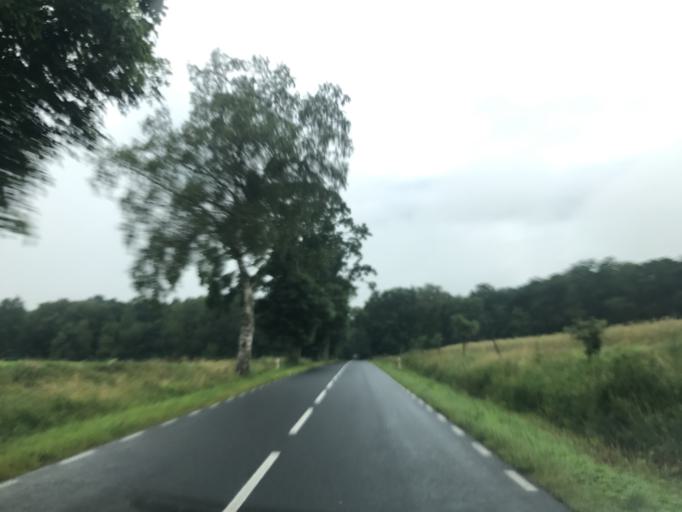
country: PL
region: West Pomeranian Voivodeship
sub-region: Powiat koszalinski
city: Bobolice
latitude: 53.9882
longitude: 16.4659
